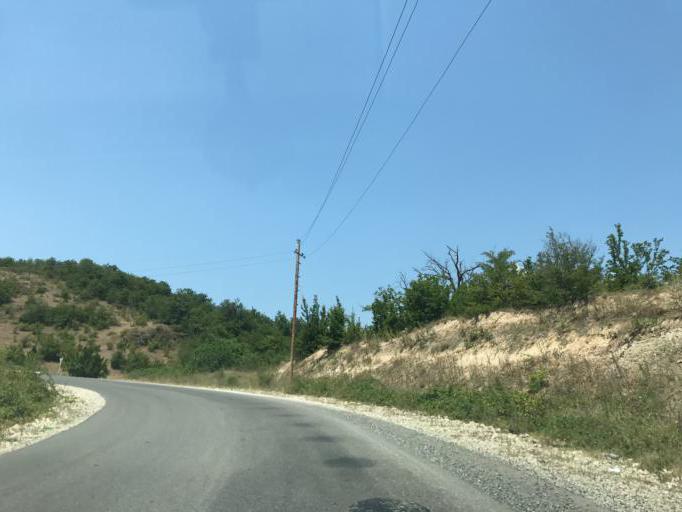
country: AZ
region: Tartar Rayon
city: Martakert
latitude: 40.1425
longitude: 46.5918
